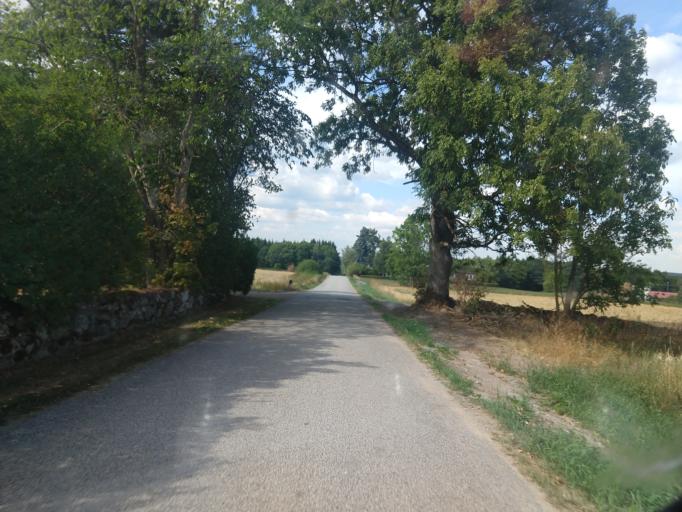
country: SE
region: Blekinge
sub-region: Karlskrona Kommun
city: Nattraby
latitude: 56.2516
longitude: 15.5265
